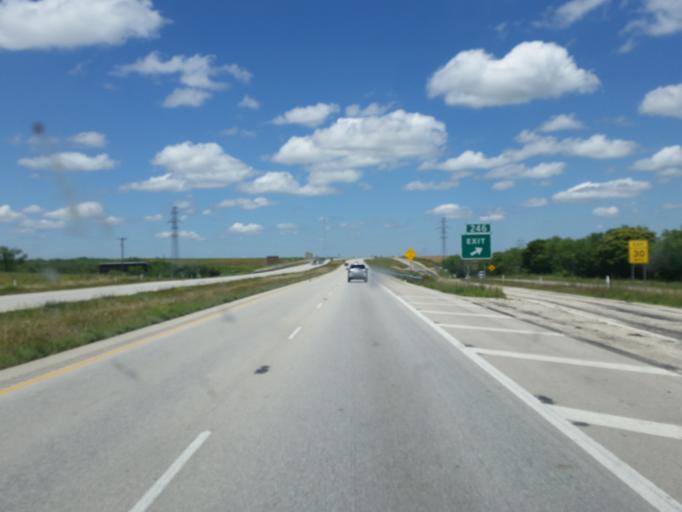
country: US
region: Texas
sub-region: Nolan County
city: Sweetwater
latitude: 32.4613
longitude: -100.3847
